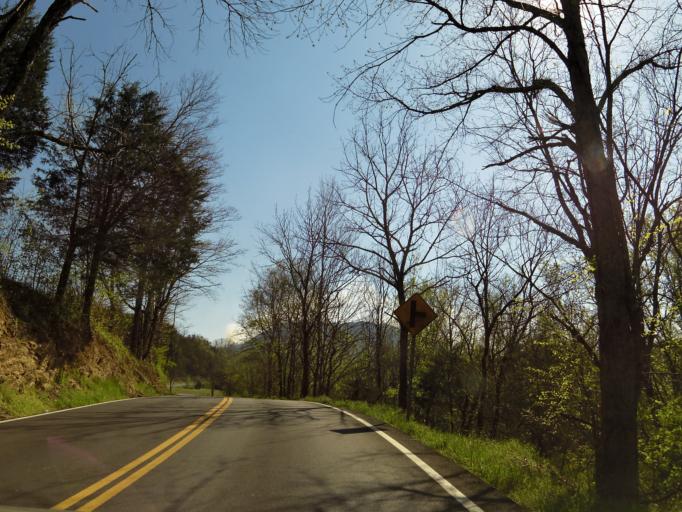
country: US
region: Tennessee
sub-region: Sevier County
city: Sevierville
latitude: 35.8412
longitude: -83.6338
